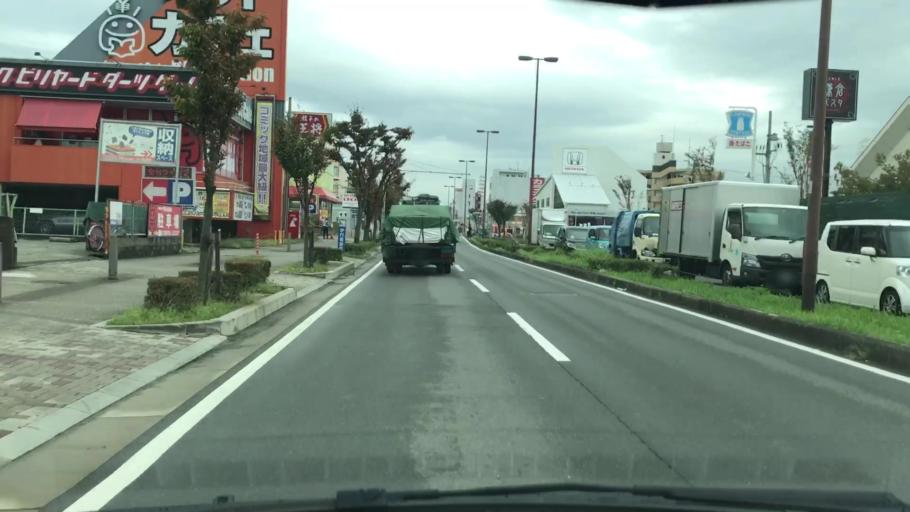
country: JP
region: Hyogo
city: Amagasaki
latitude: 34.7437
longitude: 135.4165
